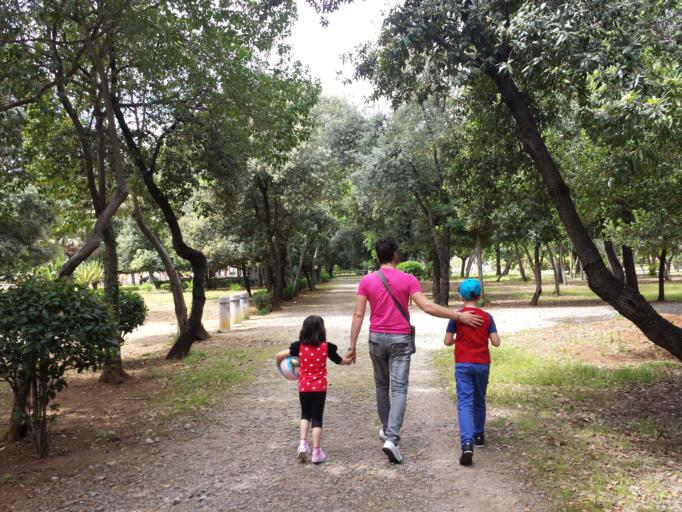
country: IT
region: Sicily
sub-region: Palermo
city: Palermo
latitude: 38.1302
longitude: 13.3477
